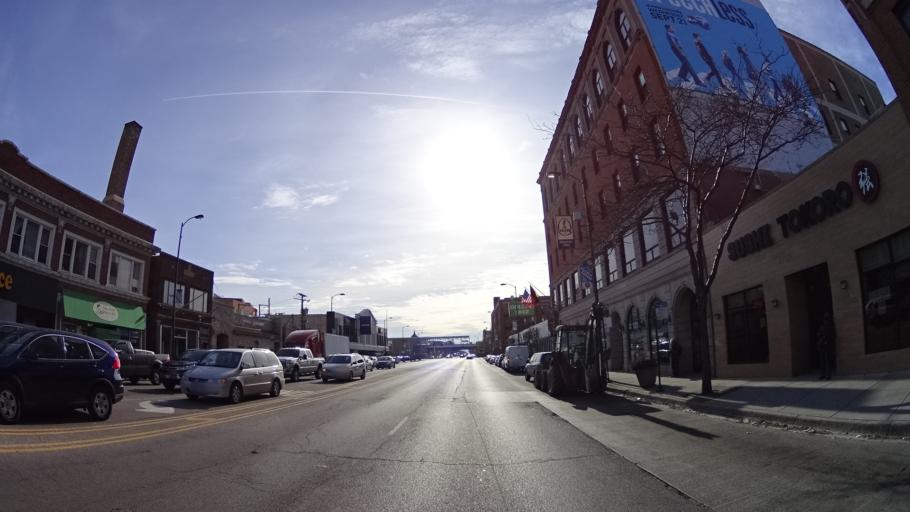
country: US
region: Illinois
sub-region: Cook County
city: Lincolnwood
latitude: 41.9684
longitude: -87.6890
